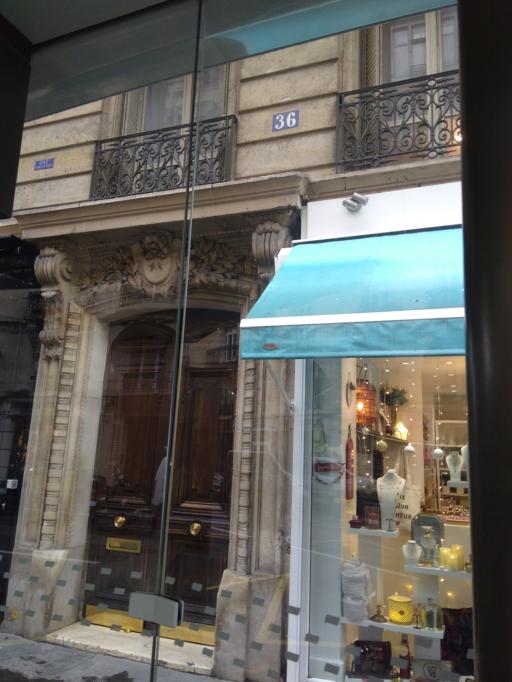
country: FR
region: Ile-de-France
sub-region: Departement des Hauts-de-Seine
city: Clichy
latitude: 48.8858
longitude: 2.3090
